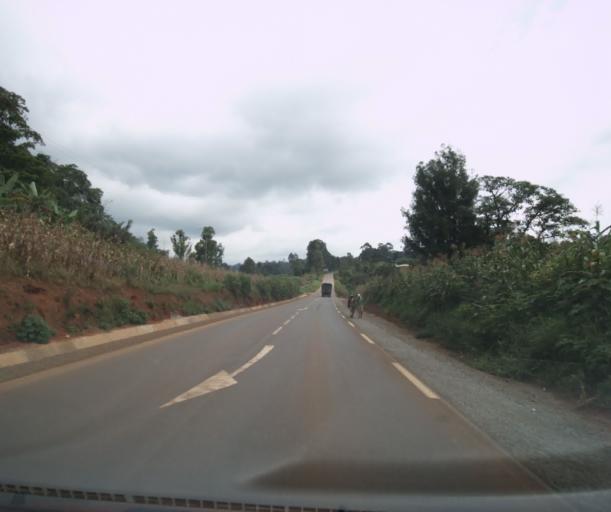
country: CM
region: West
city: Mbouda
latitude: 5.6633
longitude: 10.2223
